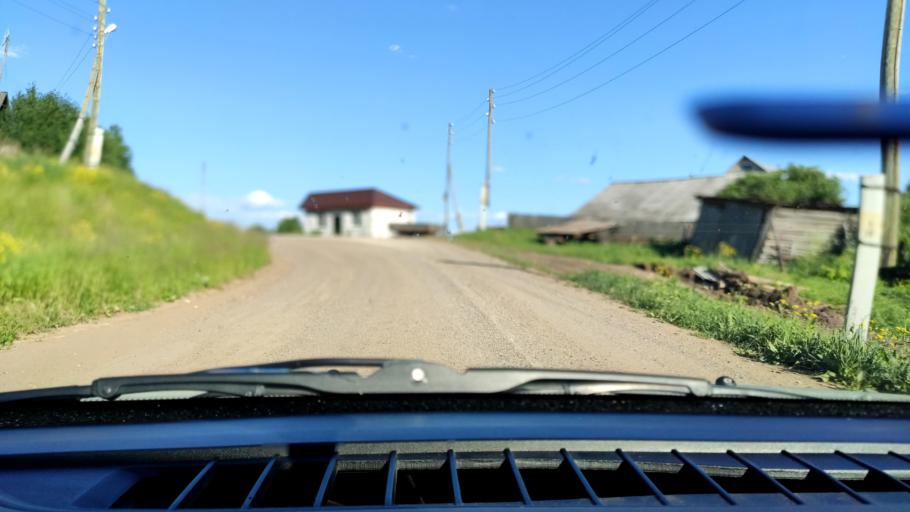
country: RU
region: Perm
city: Uinskoye
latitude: 57.1171
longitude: 56.5116
